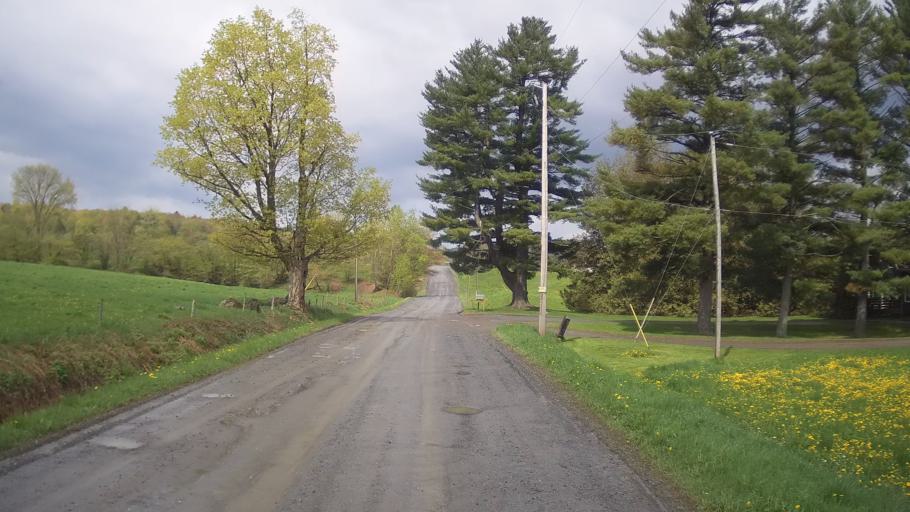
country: CA
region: Quebec
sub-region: Monteregie
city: Cowansville
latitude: 45.1736
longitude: -72.6738
